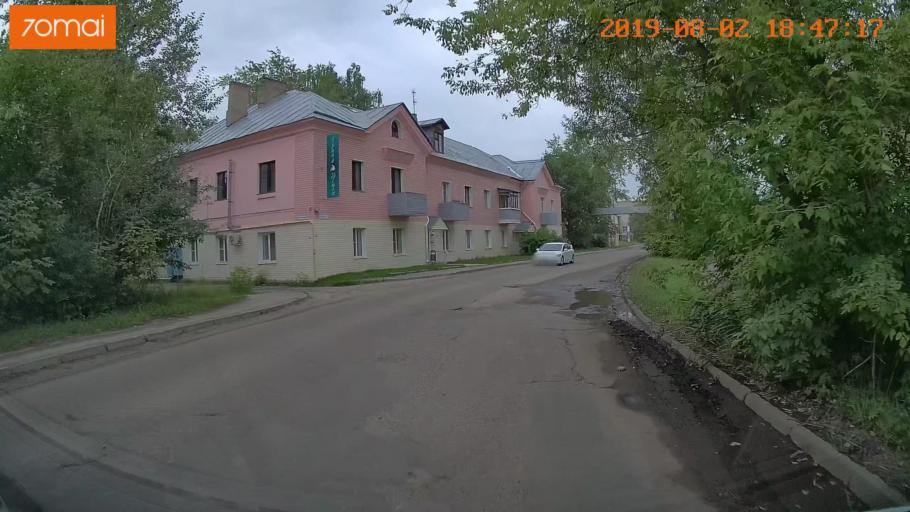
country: RU
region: Ivanovo
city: Bogorodskoye
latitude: 56.9893
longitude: 41.0417
